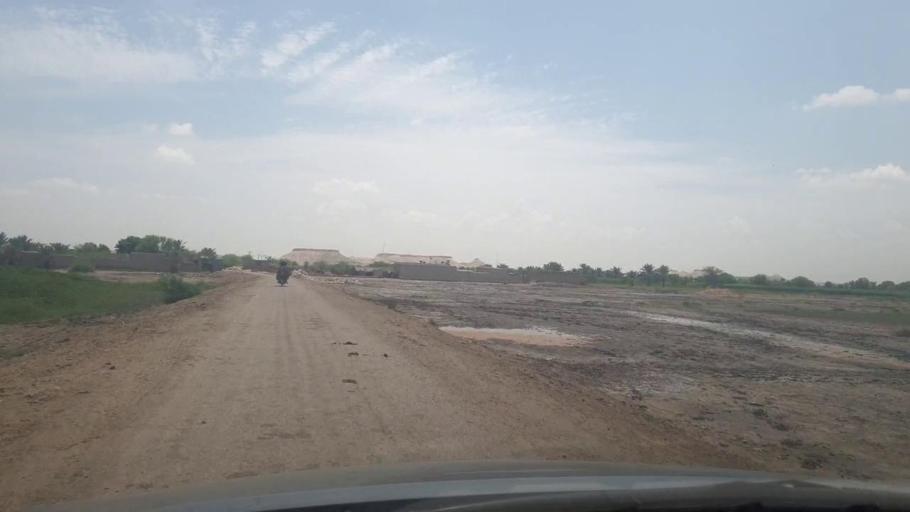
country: PK
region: Sindh
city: Kot Diji
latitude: 27.3923
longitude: 68.7627
